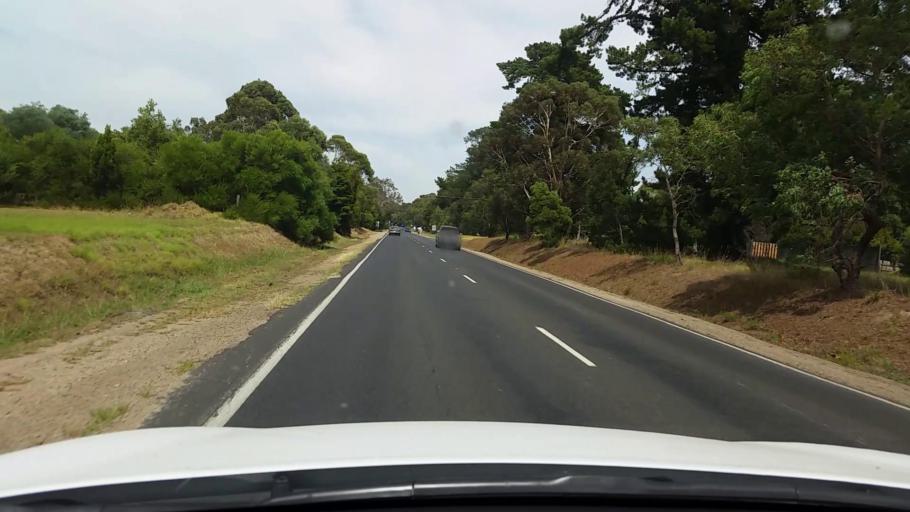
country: AU
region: Victoria
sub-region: Mornington Peninsula
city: Balnarring
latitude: -38.3706
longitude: 145.1316
